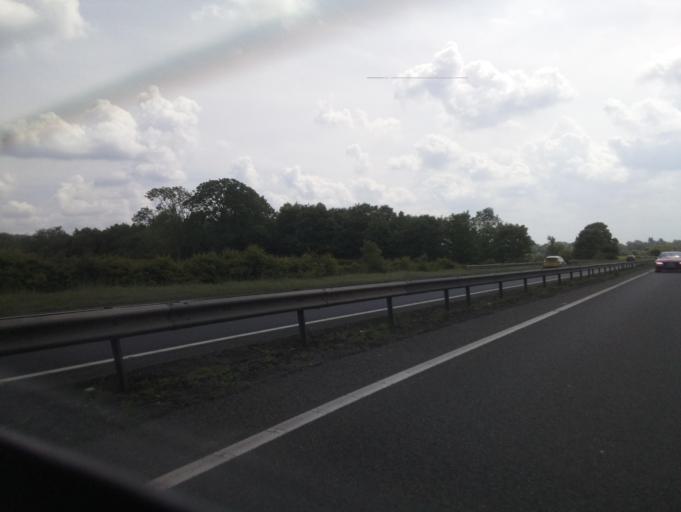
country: GB
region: England
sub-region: North Yorkshire
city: Thirsk
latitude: 54.2980
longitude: -1.3370
